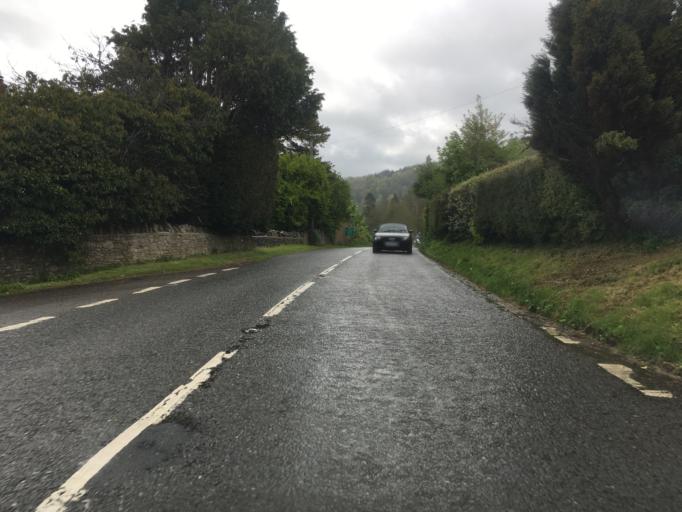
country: GB
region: England
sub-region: North Somerset
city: Burrington
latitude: 51.3316
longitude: -2.7406
